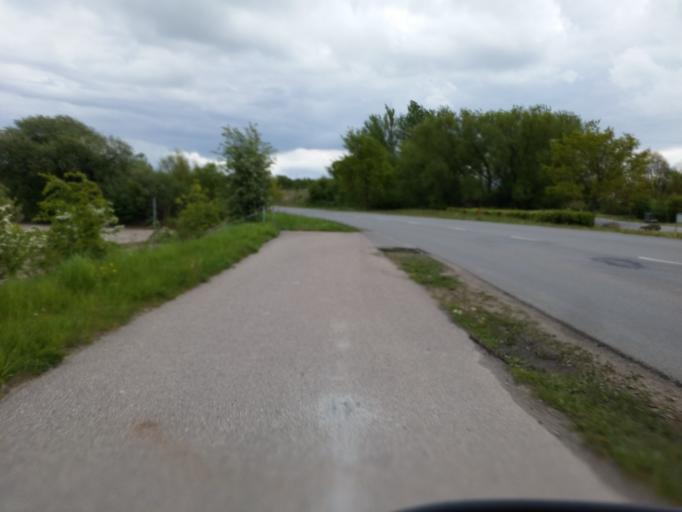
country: DK
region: South Denmark
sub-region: Kerteminde Kommune
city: Munkebo
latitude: 55.4652
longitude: 10.5421
